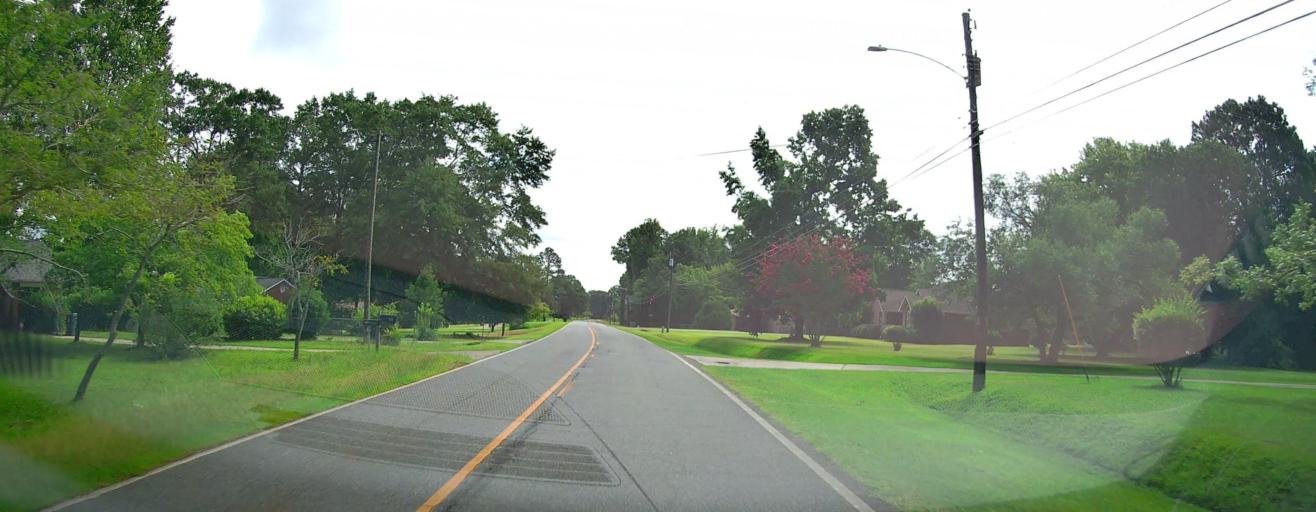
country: US
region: Georgia
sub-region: Peach County
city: Byron
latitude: 32.6469
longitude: -83.7712
